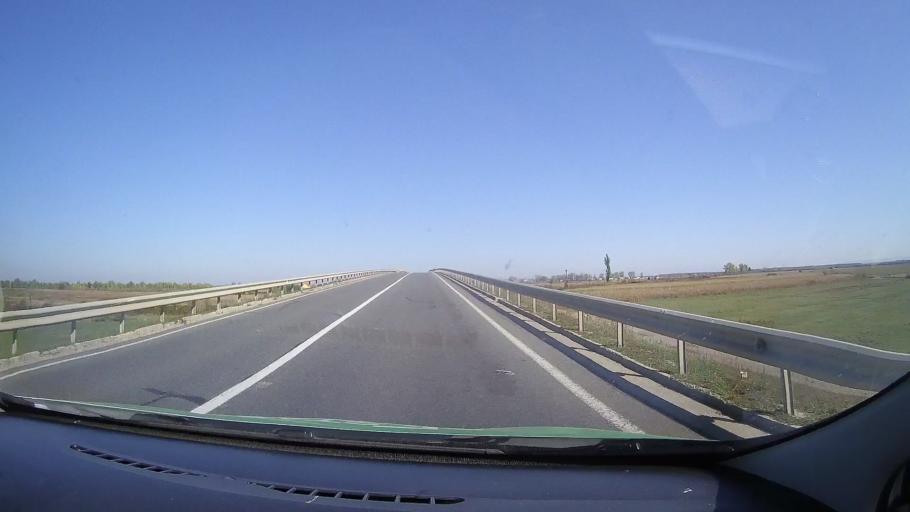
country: RO
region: Satu Mare
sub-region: Comuna Moftinu
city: Moftinu Mic
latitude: 47.6956
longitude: 22.6200
